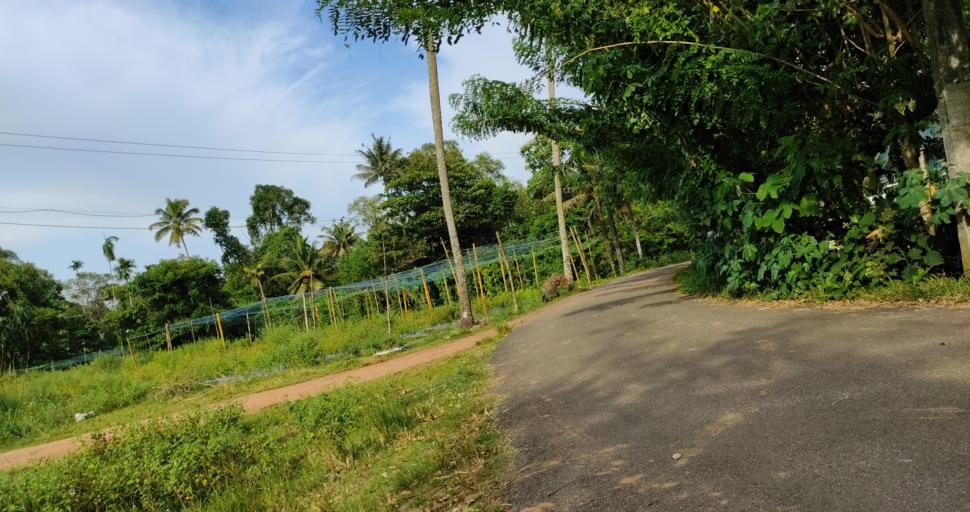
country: IN
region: Kerala
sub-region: Alappuzha
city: Shertallai
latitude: 9.6145
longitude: 76.3457
